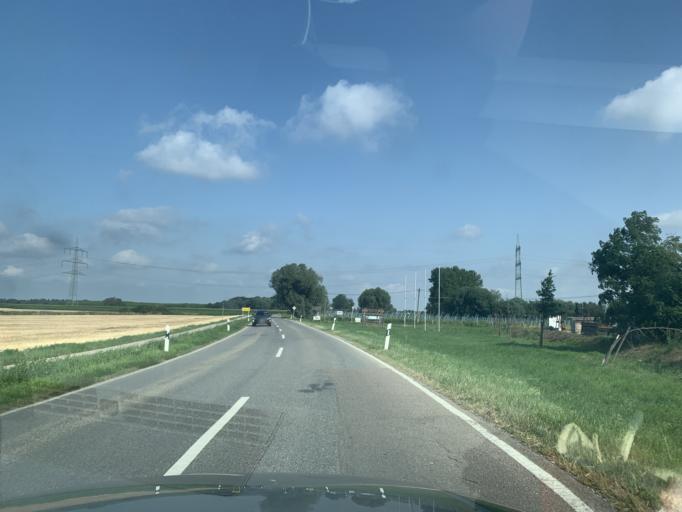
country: DE
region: Bavaria
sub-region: Swabia
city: Mering
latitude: 48.2833
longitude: 10.9840
